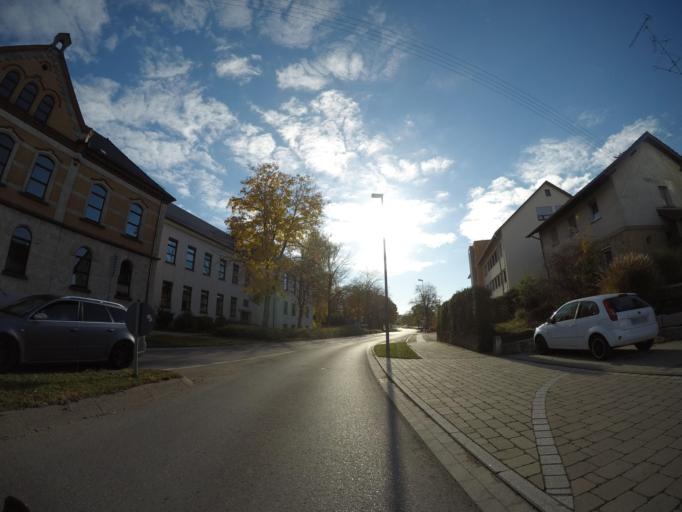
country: DE
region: Baden-Wuerttemberg
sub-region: Tuebingen Region
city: Herbertingen
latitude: 48.0594
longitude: 9.4399
